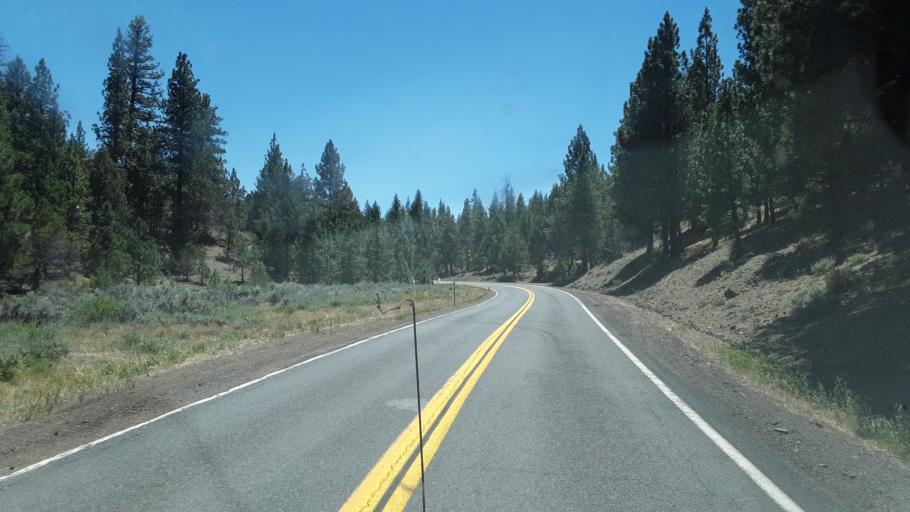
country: US
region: California
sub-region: Modoc County
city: Alturas
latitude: 41.0037
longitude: -120.8118
